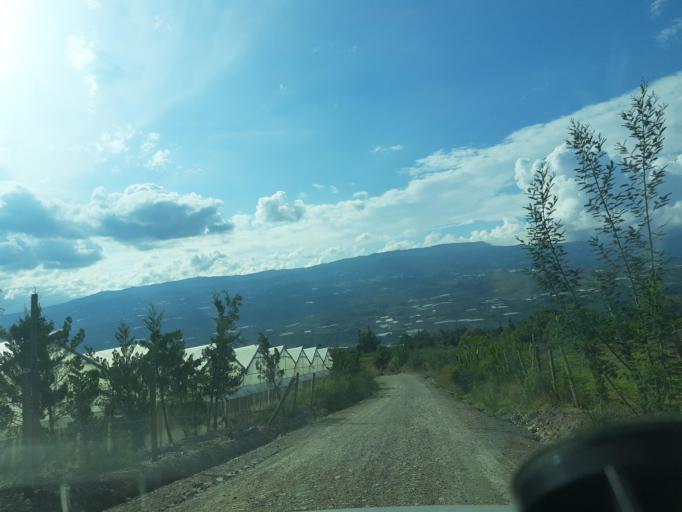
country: CO
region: Boyaca
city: Villa de Leiva
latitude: 5.6671
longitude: -73.5559
